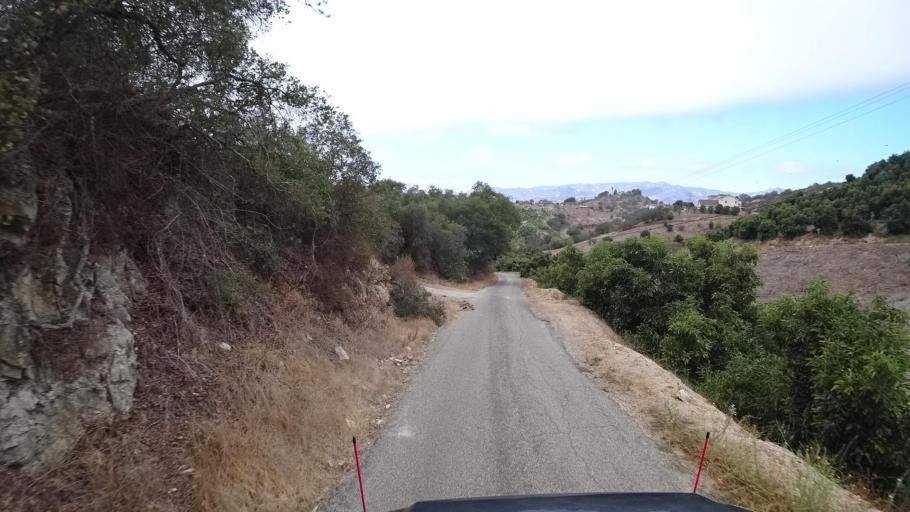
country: US
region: California
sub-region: San Diego County
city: Fallbrook
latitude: 33.4287
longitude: -117.3048
